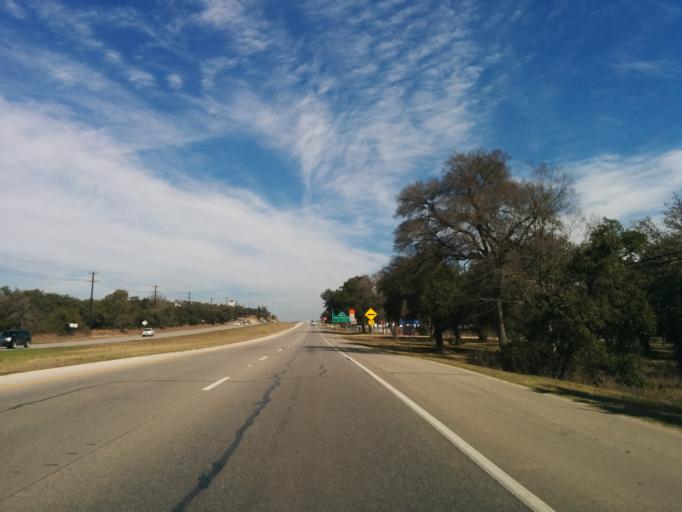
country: US
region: Texas
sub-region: Comal County
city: Bulverde
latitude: 29.7866
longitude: -98.4224
